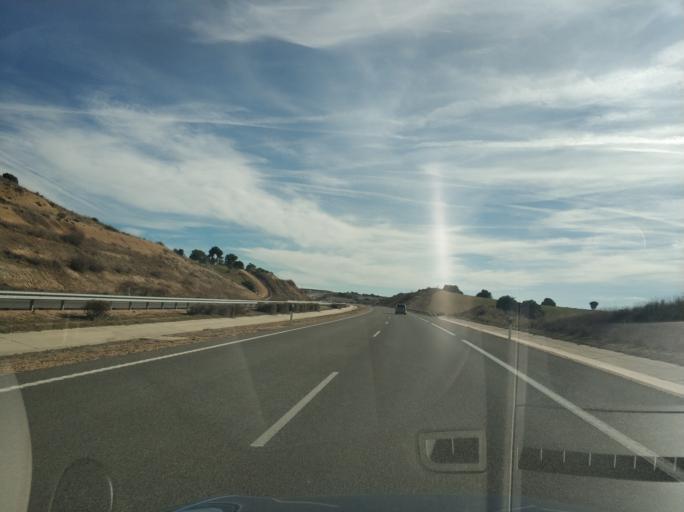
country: ES
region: Castille and Leon
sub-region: Provincia de Zamora
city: Corrales
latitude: 41.3190
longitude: -5.7235
